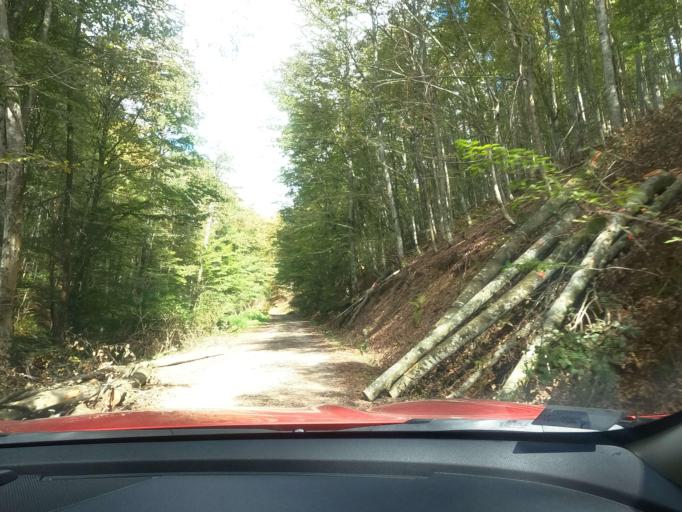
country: BA
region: Federation of Bosnia and Herzegovina
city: Velika Kladusa
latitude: 45.2429
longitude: 15.7735
